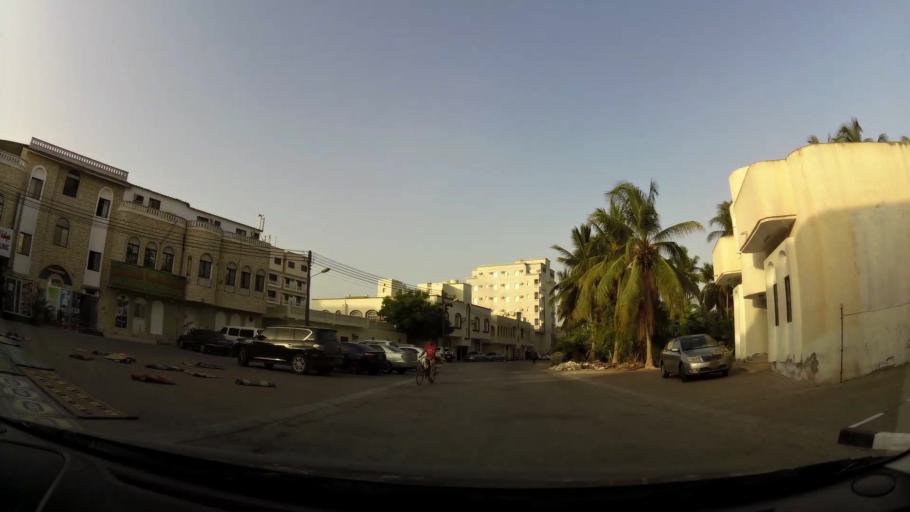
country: OM
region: Zufar
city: Salalah
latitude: 17.0138
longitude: 54.1047
